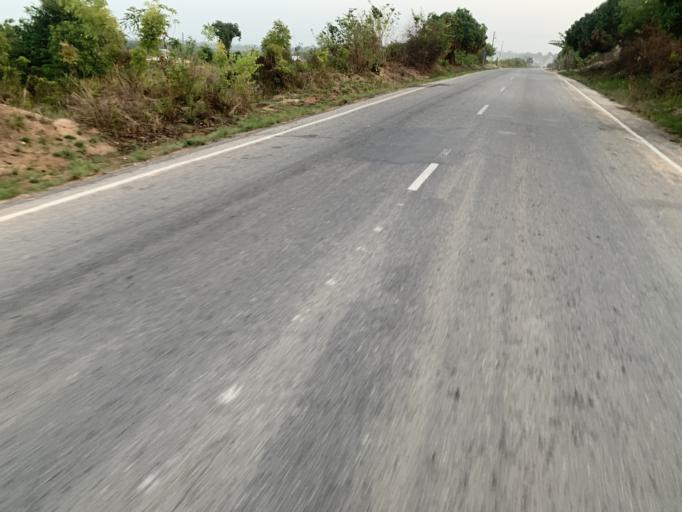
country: GH
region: Central
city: Winneba
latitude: 5.3706
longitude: -0.6074
